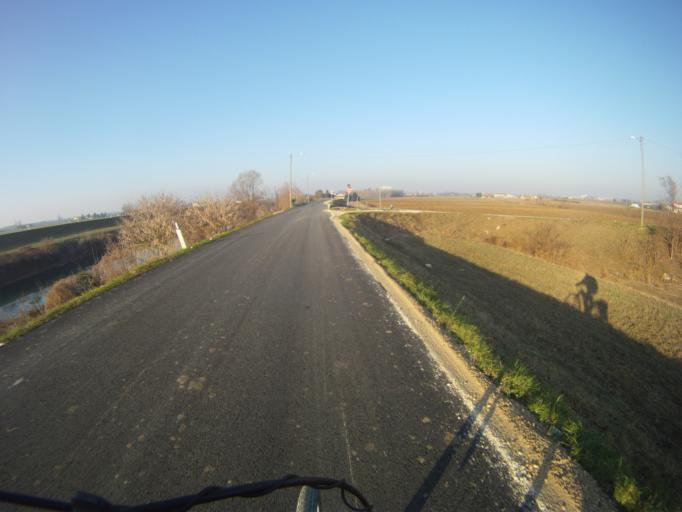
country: IT
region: Veneto
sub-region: Provincia di Padova
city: Polverara
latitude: 45.3296
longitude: 11.9392
